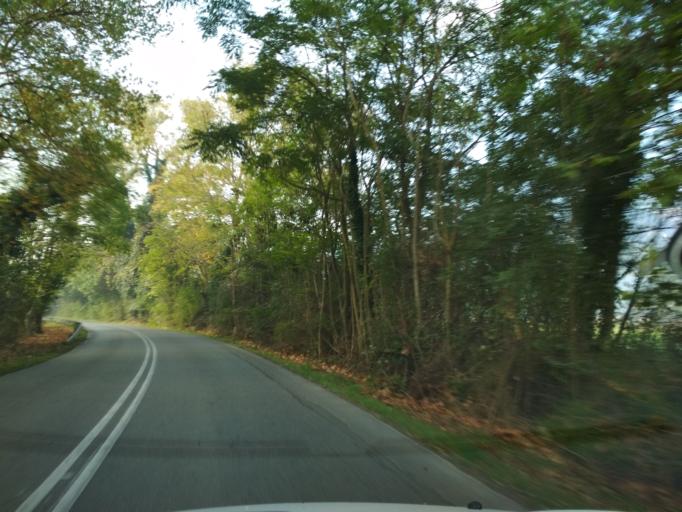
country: GR
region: Central Greece
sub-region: Nomos Evvoias
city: Prokopion
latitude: 38.7436
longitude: 23.4892
